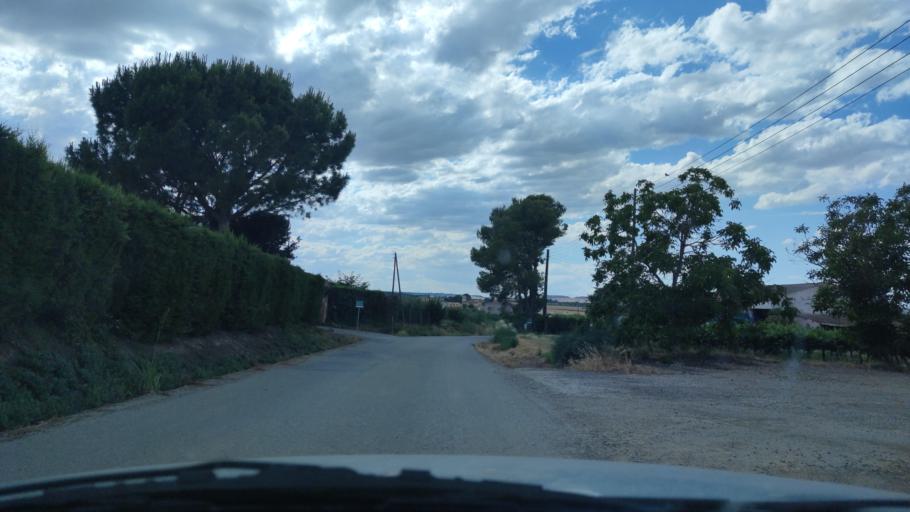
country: ES
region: Catalonia
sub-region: Provincia de Lleida
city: Lleida
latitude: 41.5960
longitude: 0.5713
